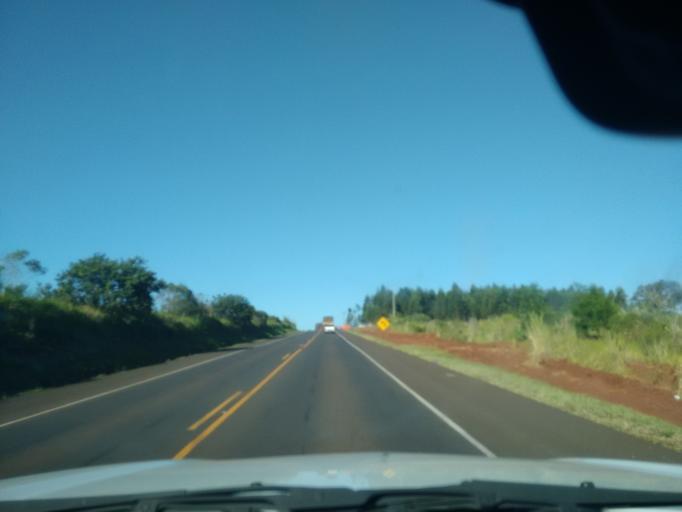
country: PY
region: Canindeyu
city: Salto del Guaira
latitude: -23.9644
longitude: -54.3239
